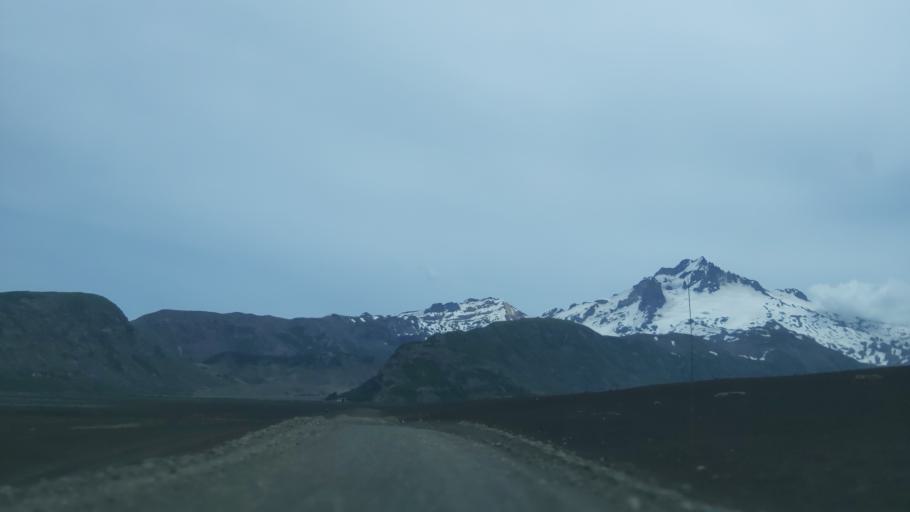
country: AR
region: Neuquen
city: Andacollo
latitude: -37.4574
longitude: -71.2983
